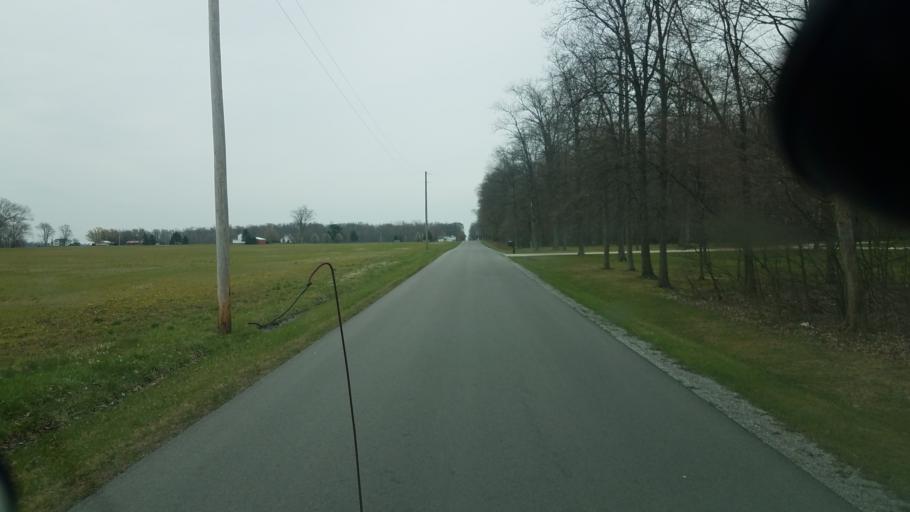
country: US
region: Ohio
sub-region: Seneca County
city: Fostoria
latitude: 41.0501
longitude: -83.4720
